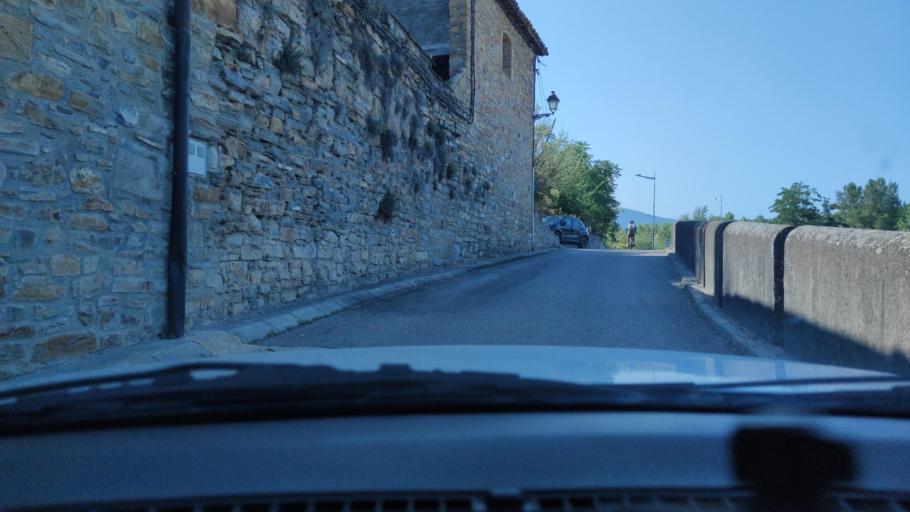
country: ES
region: Catalonia
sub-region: Provincia de Lleida
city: Senterada
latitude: 42.2436
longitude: 0.9715
